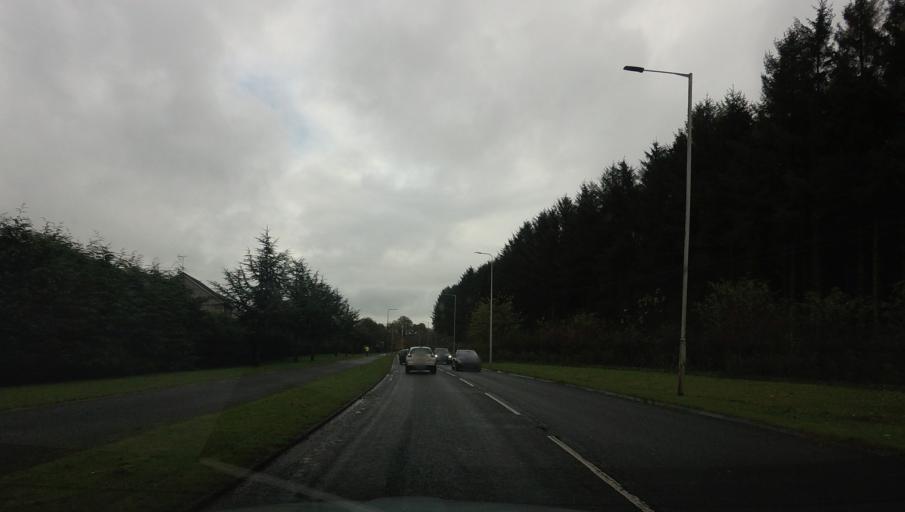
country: GB
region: Scotland
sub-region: Fife
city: Kirkcaldy
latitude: 56.1224
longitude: -3.2047
